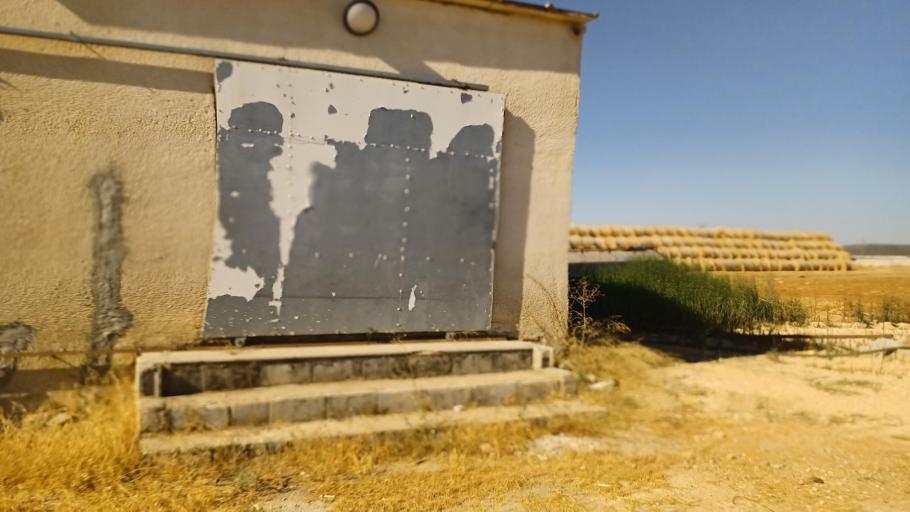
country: CY
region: Larnaka
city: Pergamos
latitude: 35.0531
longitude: 33.6896
